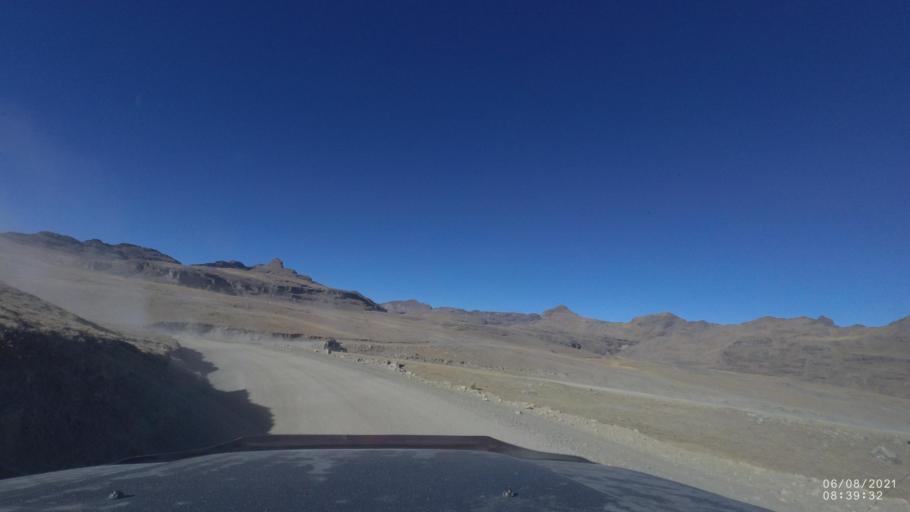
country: BO
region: Cochabamba
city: Sipe Sipe
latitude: -17.1748
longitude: -66.3988
